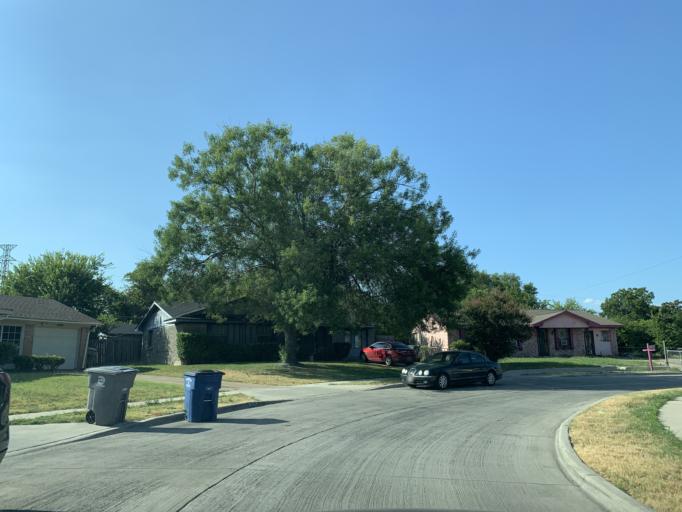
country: US
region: Texas
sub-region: Dallas County
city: Hutchins
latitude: 32.6632
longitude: -96.7690
